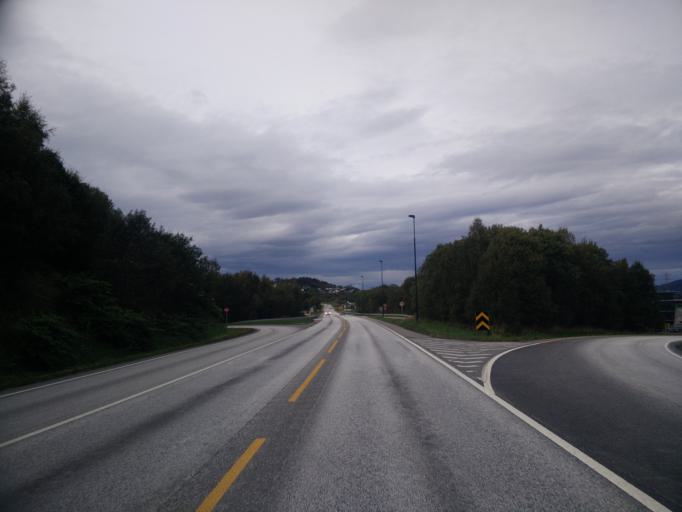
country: NO
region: More og Romsdal
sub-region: Haram
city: Brattvag
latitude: 62.4710
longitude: 6.3684
